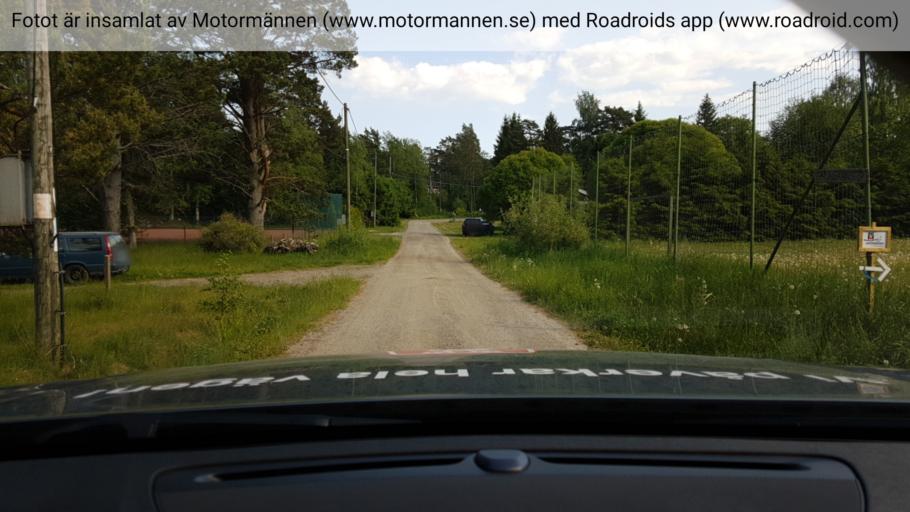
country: SE
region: Stockholm
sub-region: Varmdo Kommun
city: Mortnas
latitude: 59.2465
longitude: 18.4595
